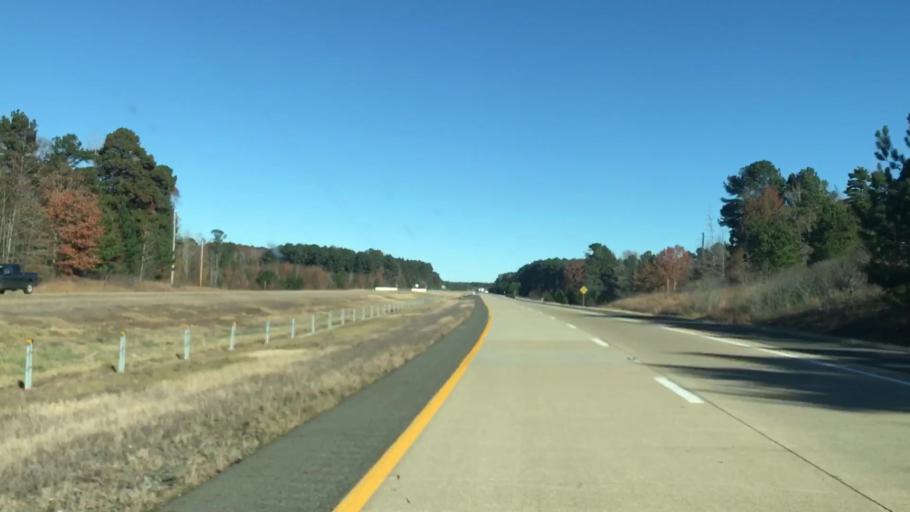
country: US
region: Louisiana
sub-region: Caddo Parish
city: Vivian
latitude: 33.0895
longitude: -93.8946
